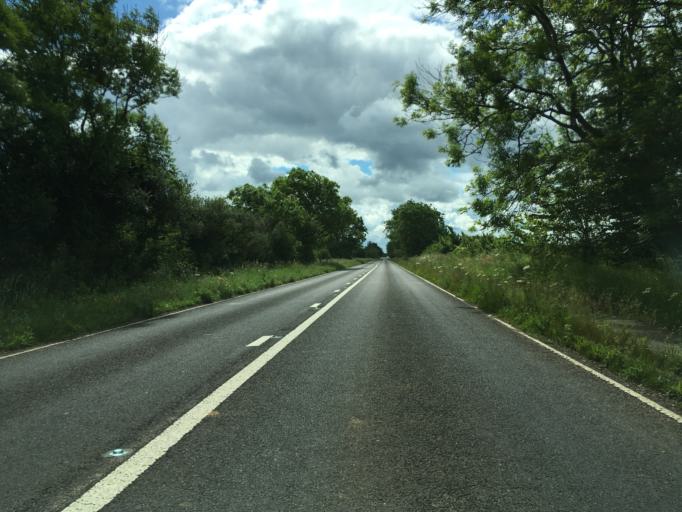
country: GB
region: England
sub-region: Oxfordshire
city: Chipping Norton
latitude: 51.9473
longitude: -1.5191
